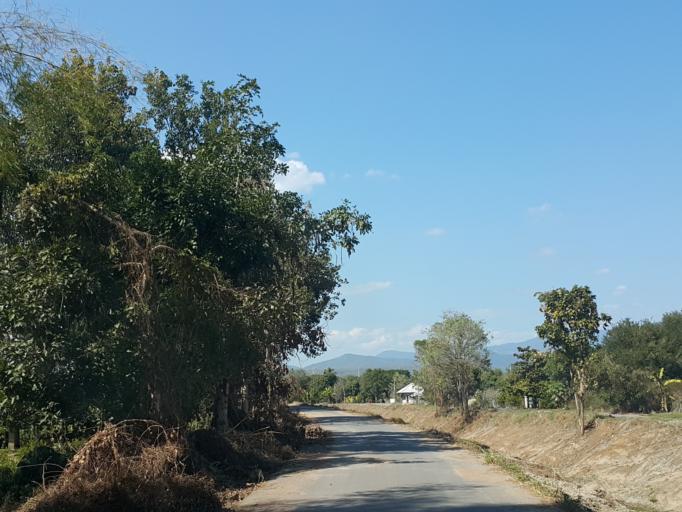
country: TH
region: Chiang Mai
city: Mae Taeng
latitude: 19.0991
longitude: 98.9394
